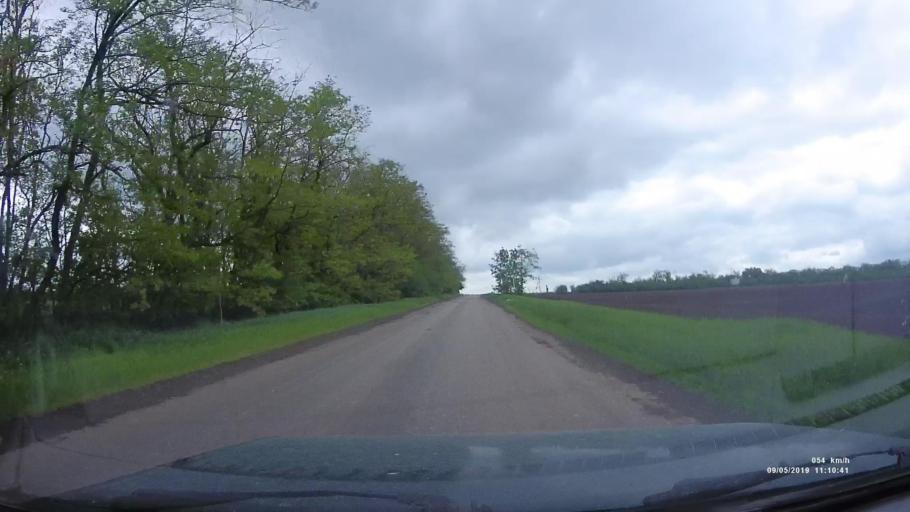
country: RU
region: Krasnodarskiy
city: Kanelovskaya
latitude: 46.7735
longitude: 39.2115
